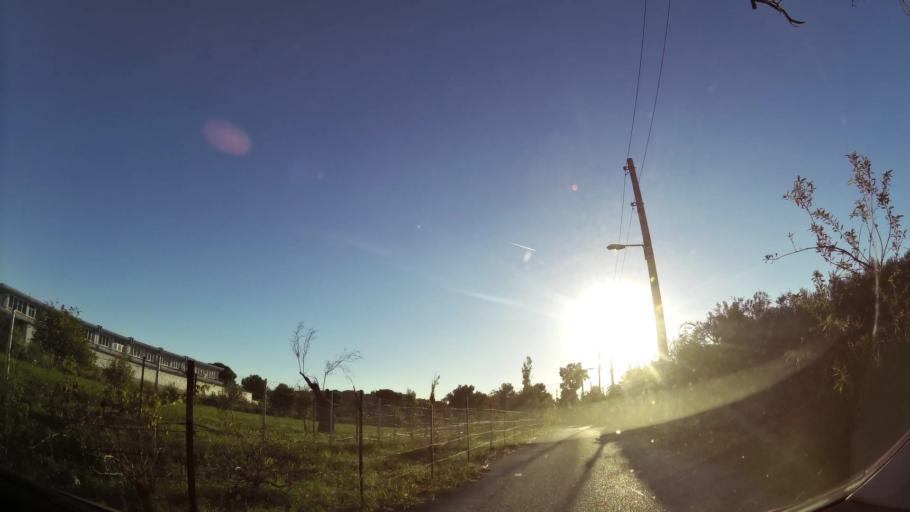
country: GR
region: Attica
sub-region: Nomarchia Anatolikis Attikis
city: Pallini
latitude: 38.0015
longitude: 23.8656
